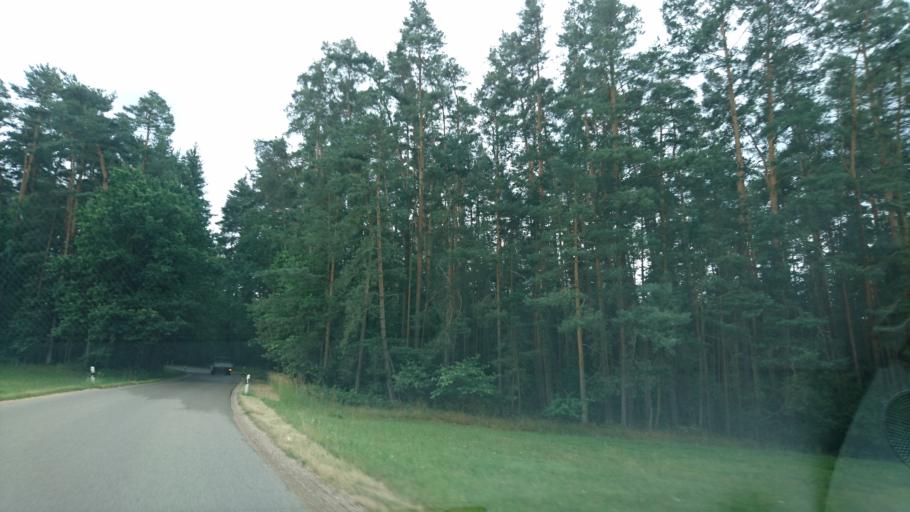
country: DE
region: Bavaria
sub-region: Regierungsbezirk Mittelfranken
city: Roth
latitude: 49.1992
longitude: 11.0943
